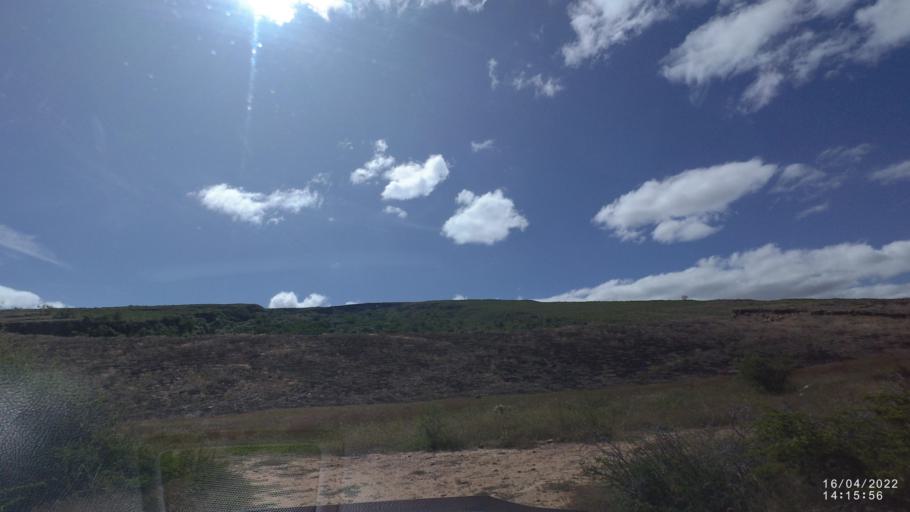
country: BO
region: Cochabamba
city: Mizque
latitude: -18.0554
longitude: -65.5106
